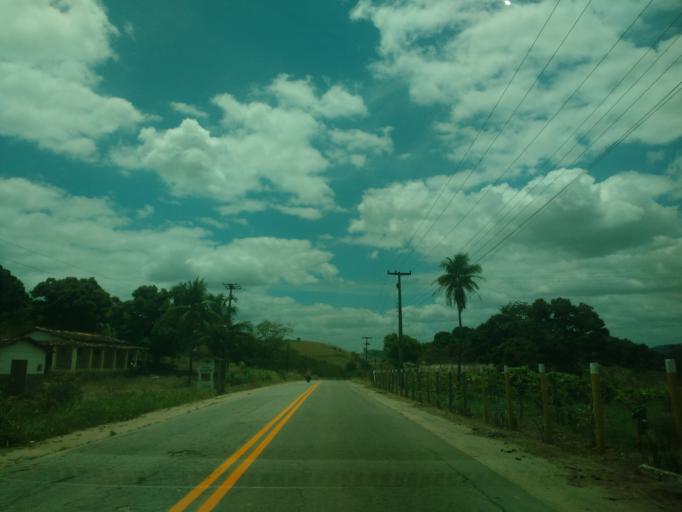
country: BR
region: Alagoas
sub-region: Uniao Dos Palmares
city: Uniao dos Palmares
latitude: -9.1422
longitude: -36.0489
